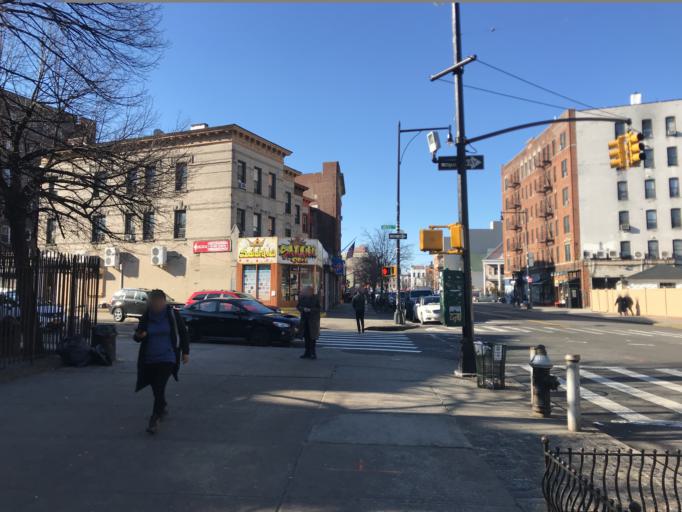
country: US
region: New York
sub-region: Kings County
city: Brooklyn
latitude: 40.6405
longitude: -73.9660
